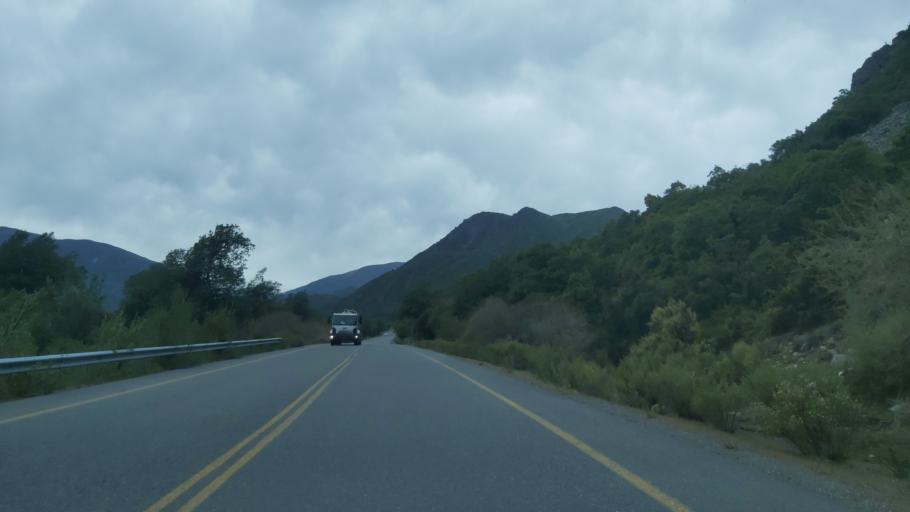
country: CL
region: Maule
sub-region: Provincia de Linares
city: Colbun
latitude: -35.8077
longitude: -70.8828
